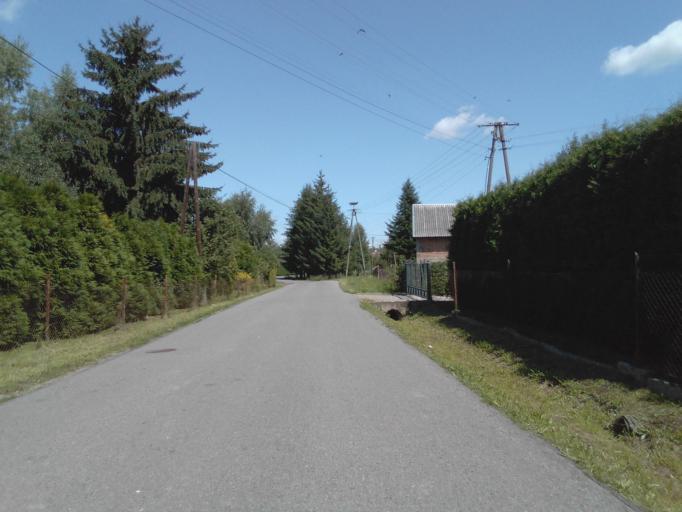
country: PL
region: Subcarpathian Voivodeship
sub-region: Powiat krosnienski
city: Jedlicze
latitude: 49.7433
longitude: 21.6332
